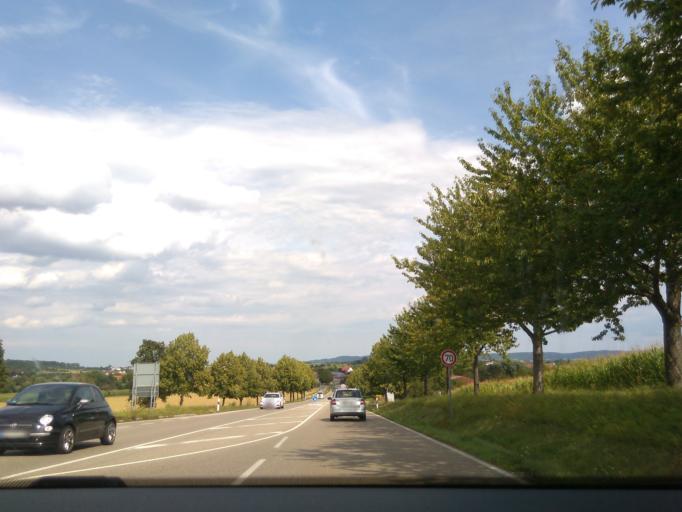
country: DE
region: Baden-Wuerttemberg
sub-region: Regierungsbezirk Stuttgart
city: Michelfeld
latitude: 49.0958
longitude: 9.6653
